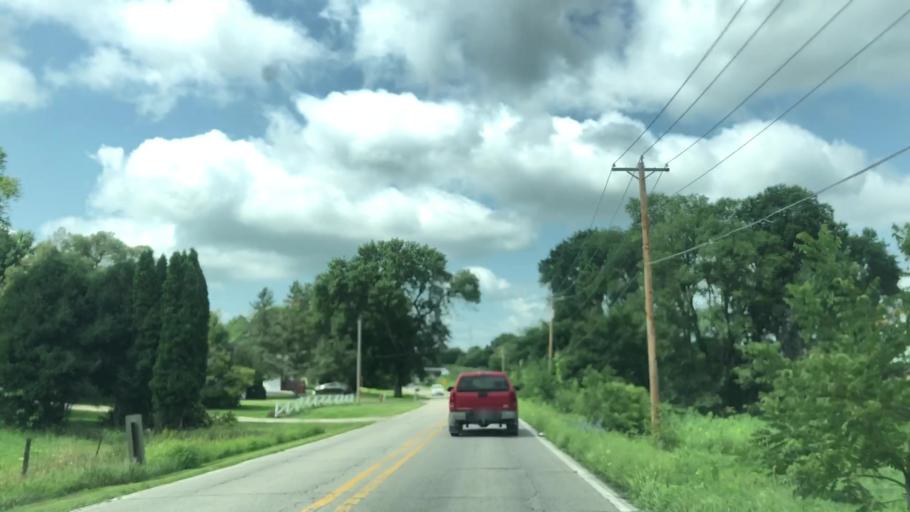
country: US
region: Iowa
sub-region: Marshall County
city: Marshalltown
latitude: 42.0527
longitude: -92.9504
